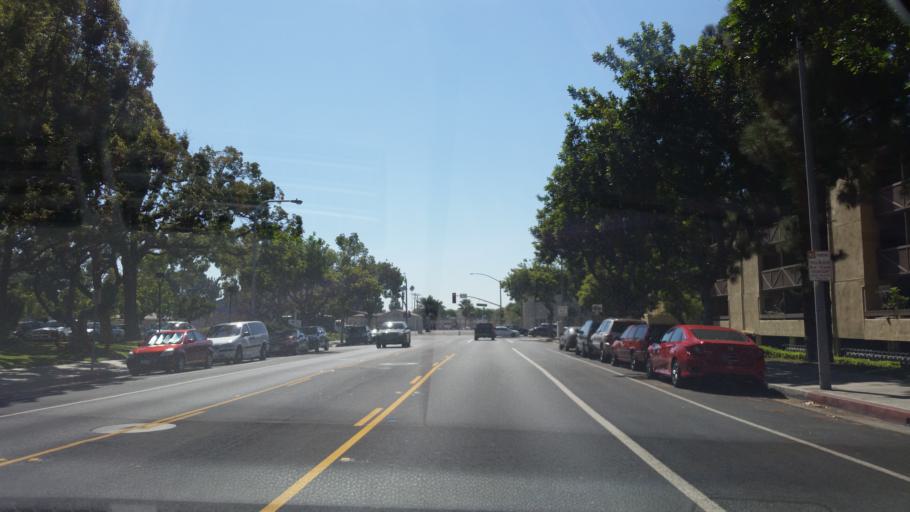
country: US
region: California
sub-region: Orange County
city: Santa Ana
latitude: 33.7465
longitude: -117.8725
